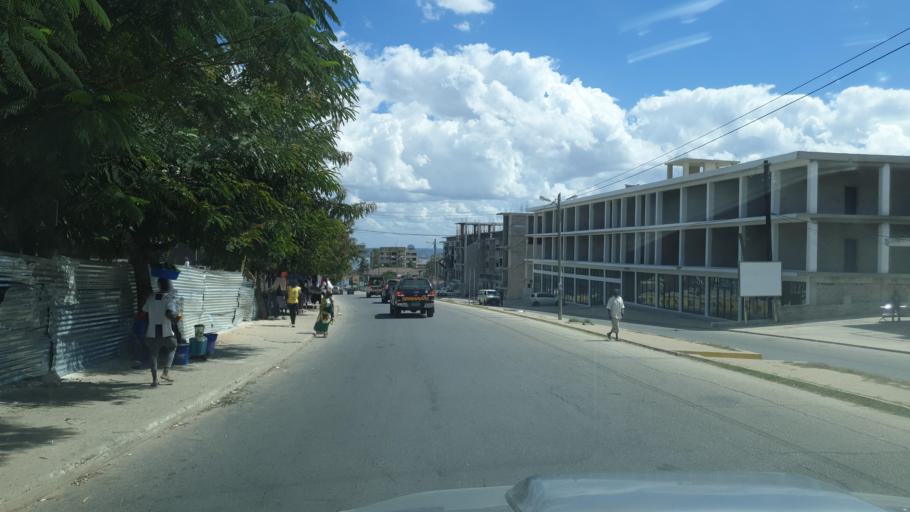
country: MZ
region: Nampula
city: Nacala
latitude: -14.5437
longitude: 40.6811
